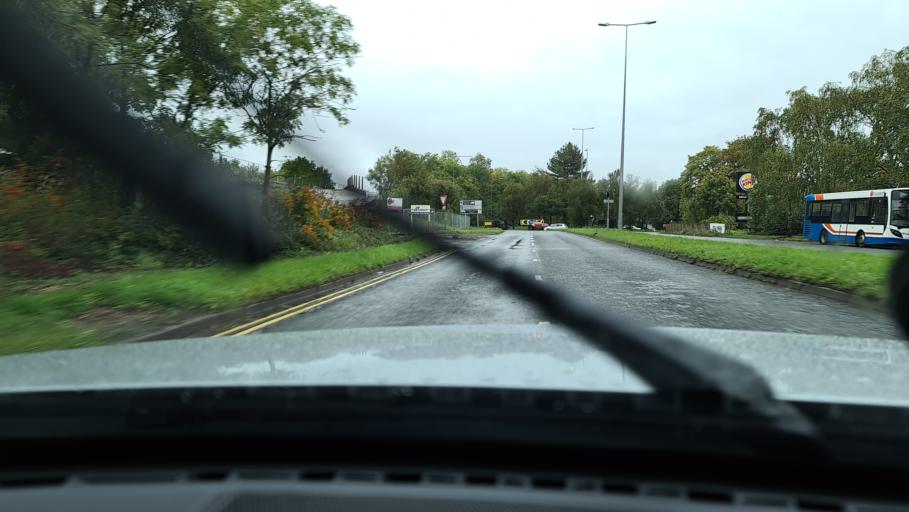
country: GB
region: England
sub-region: Buckinghamshire
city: Bletchley
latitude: 51.9958
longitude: -0.7346
